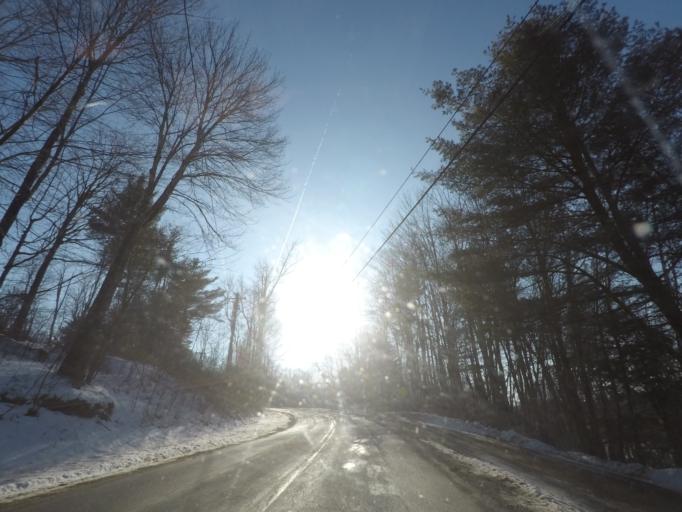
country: US
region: Massachusetts
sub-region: Berkshire County
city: Richmond
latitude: 42.5343
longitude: -73.4028
